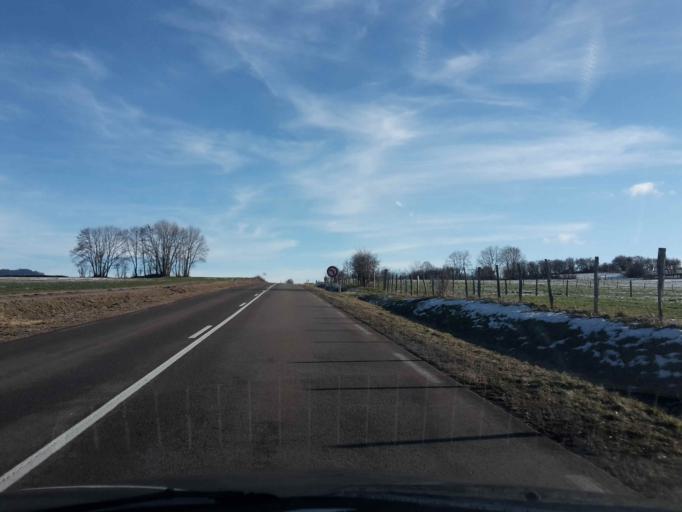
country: FR
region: Franche-Comte
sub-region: Departement du Doubs
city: Valdahon
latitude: 47.1150
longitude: 6.3135
